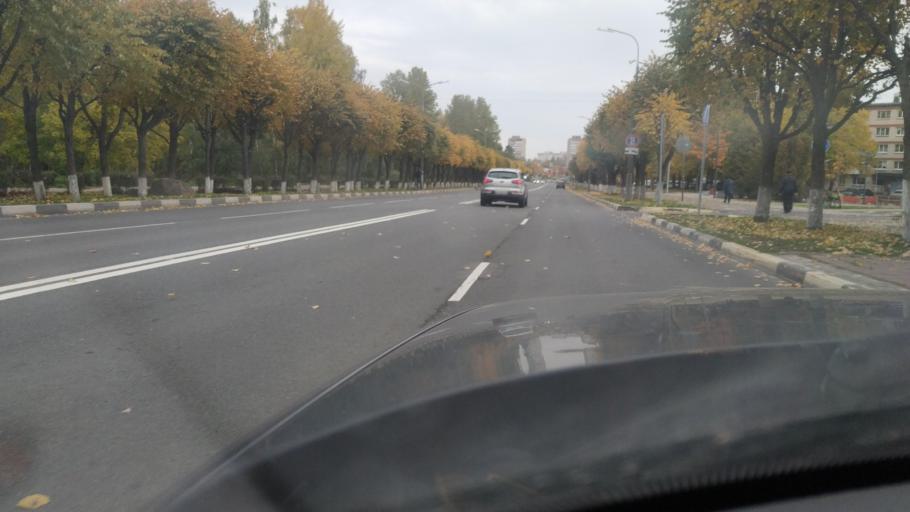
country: RU
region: Leningrad
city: Sosnovyy Bor
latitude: 59.9011
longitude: 29.0883
